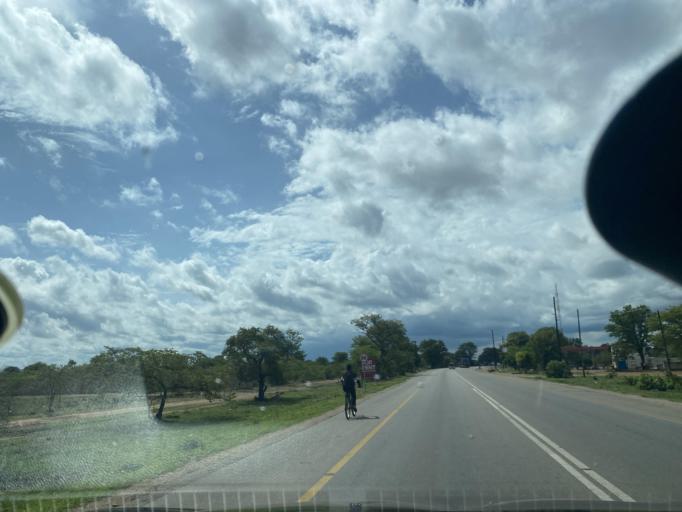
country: ZM
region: Lusaka
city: Kafue
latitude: -15.8539
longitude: 28.2538
